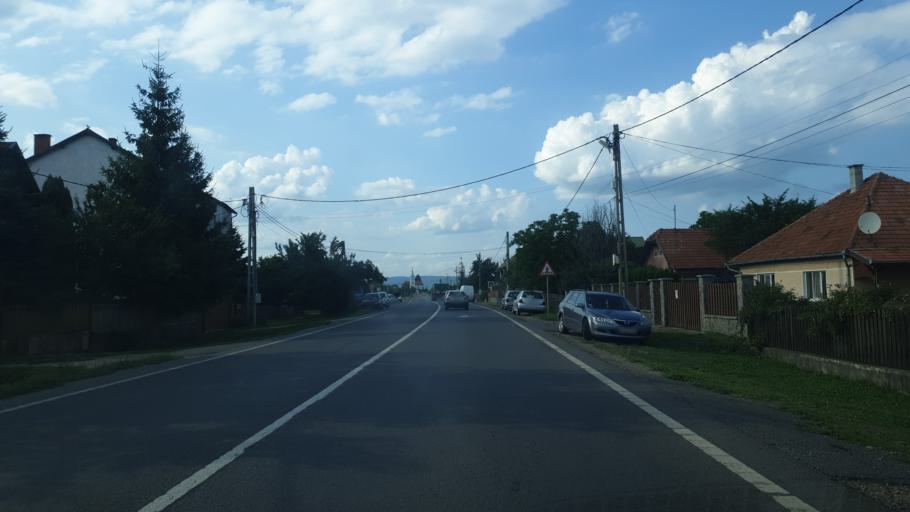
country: RO
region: Covasna
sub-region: Municipiul Sfantu Gheorghe
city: Sfantu-Gheorghe
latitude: 45.8351
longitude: 25.8044
